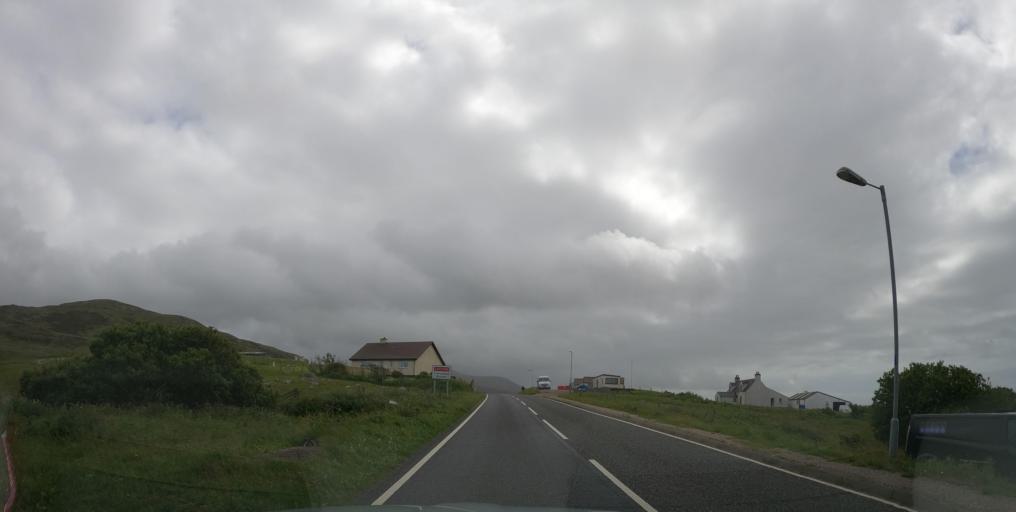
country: GB
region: Scotland
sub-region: Eilean Siar
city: Isle of South Uist
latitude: 57.2997
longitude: -7.3688
